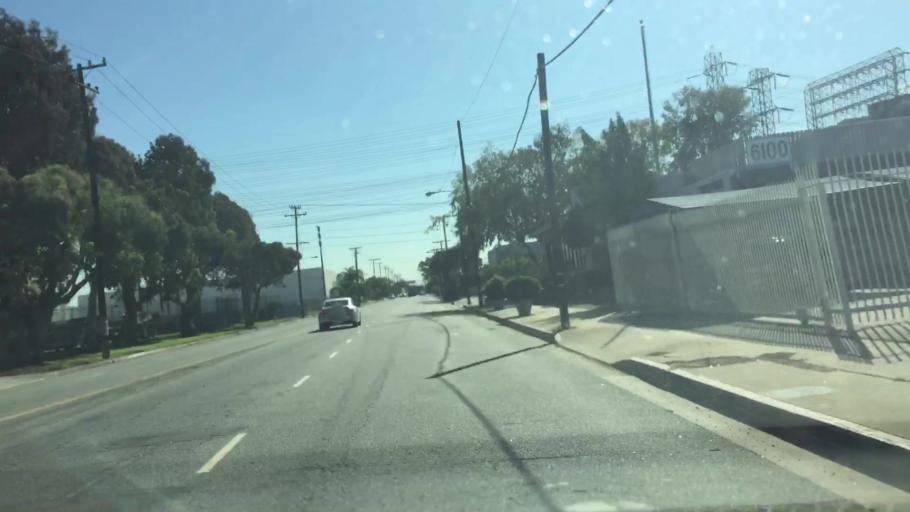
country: US
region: California
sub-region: Los Angeles County
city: Commerce
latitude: 33.9900
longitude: -118.1508
